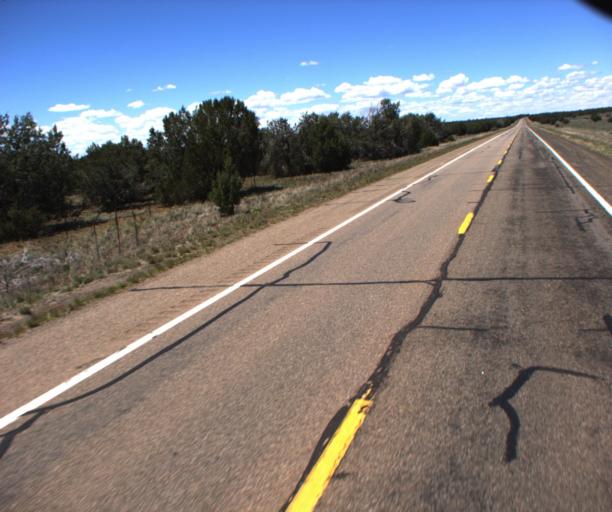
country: US
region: Arizona
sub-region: Yavapai County
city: Paulden
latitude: 35.1512
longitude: -112.4502
